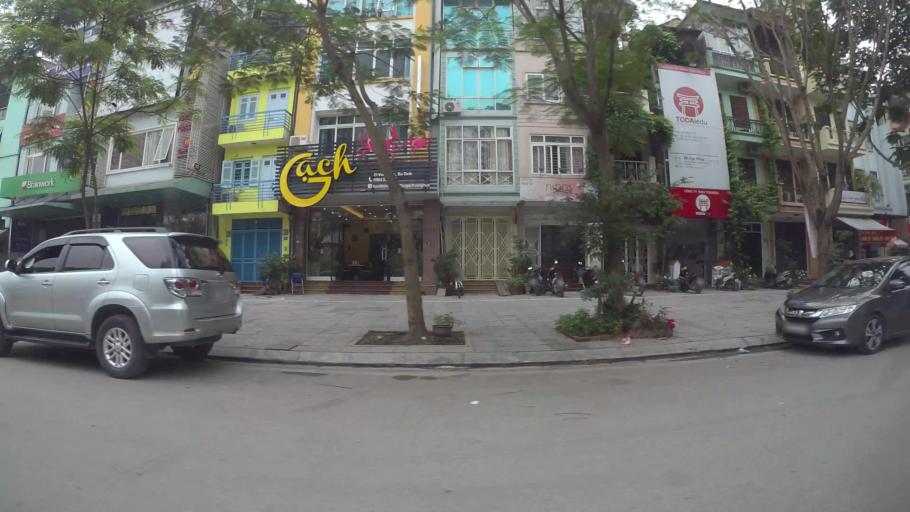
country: VN
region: Ha Noi
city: Dong Da
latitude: 21.0333
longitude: 105.8193
